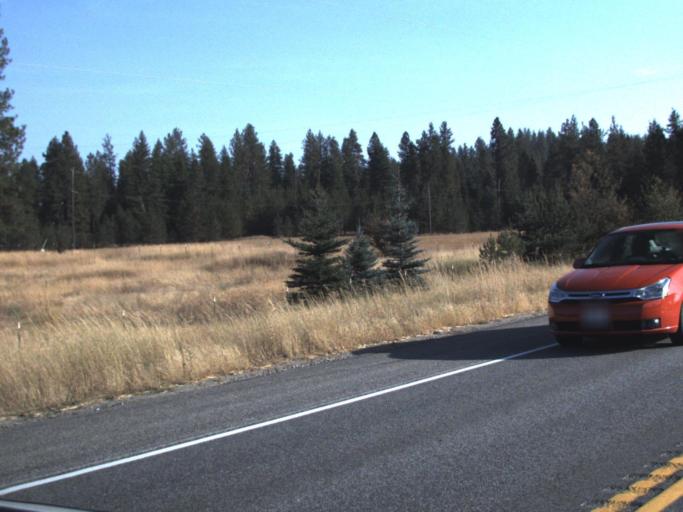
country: US
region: Washington
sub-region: Spokane County
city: Deer Park
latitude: 47.9328
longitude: -117.3513
